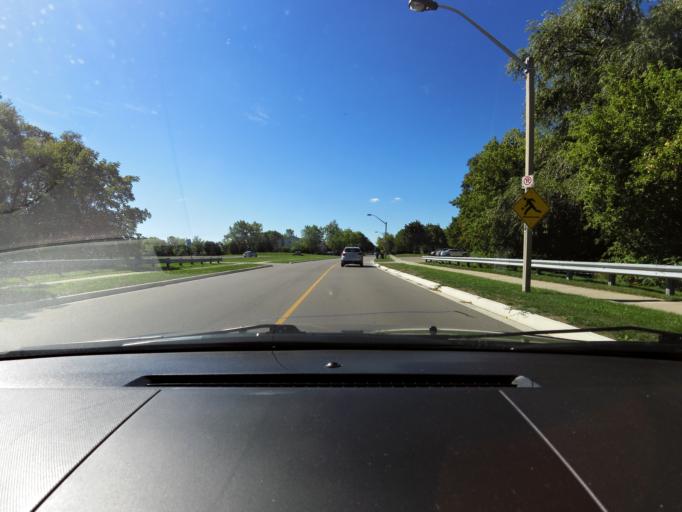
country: CA
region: Ontario
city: Burlington
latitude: 43.3744
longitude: -79.8015
